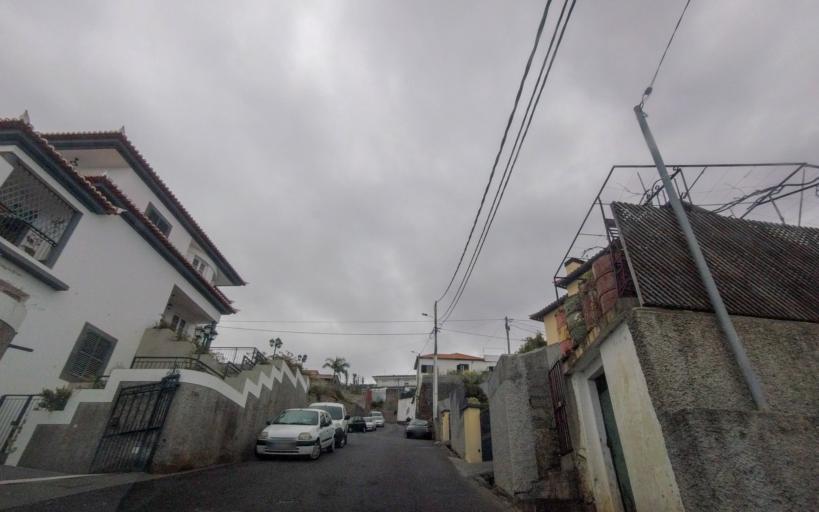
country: PT
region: Madeira
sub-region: Funchal
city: Nossa Senhora do Monte
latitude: 32.6614
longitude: -16.8859
